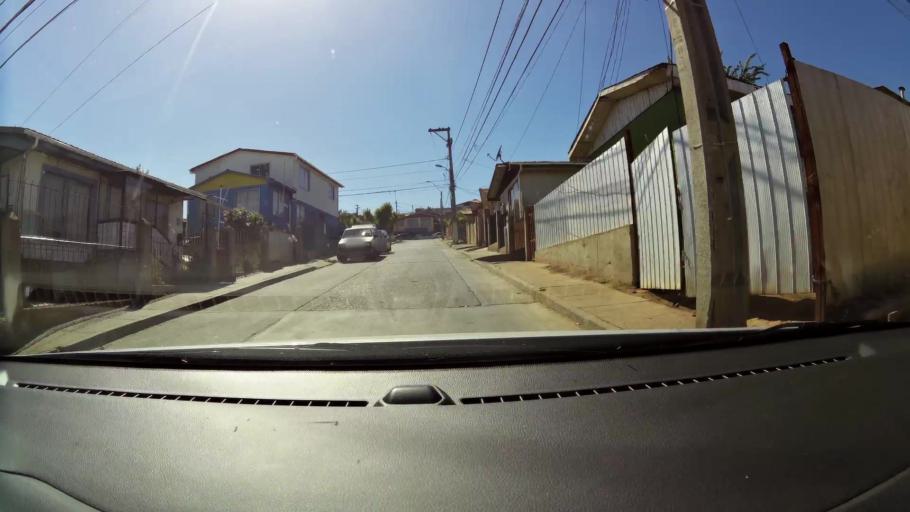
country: CL
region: Valparaiso
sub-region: Provincia de Valparaiso
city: Vina del Mar
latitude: -33.0599
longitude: -71.5781
